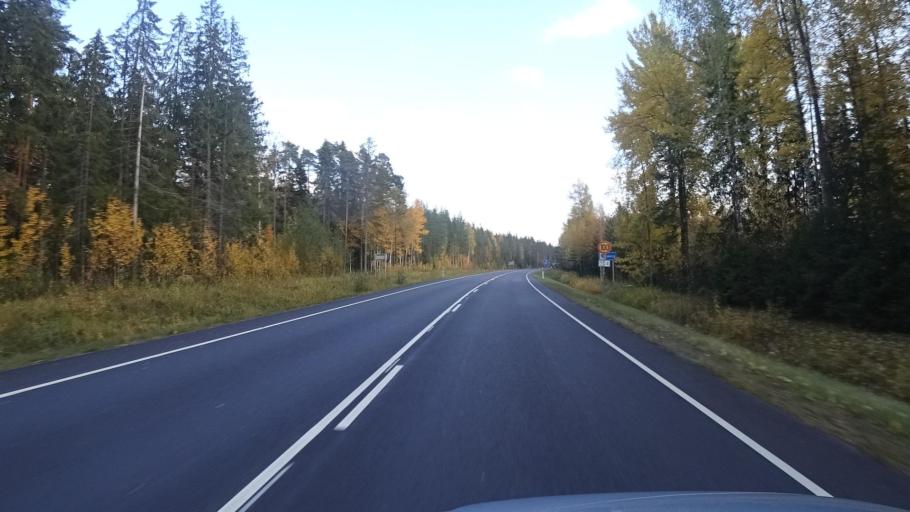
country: FI
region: Satakunta
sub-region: Rauma
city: Koeylioe
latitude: 61.1053
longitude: 22.2261
